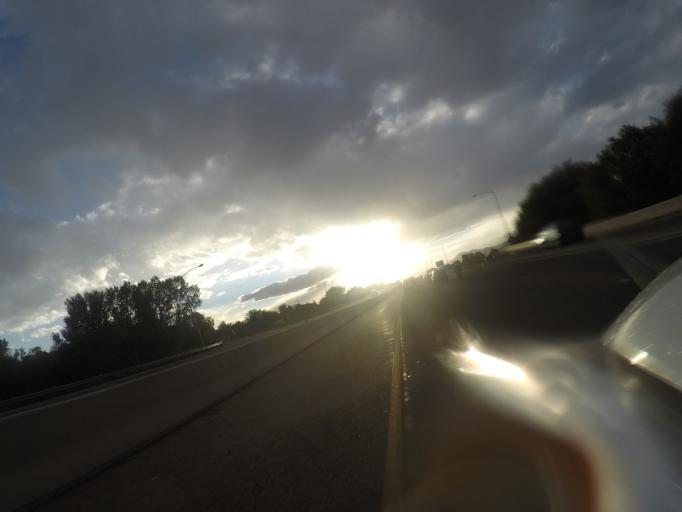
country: US
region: Colorado
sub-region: Arapahoe County
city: Sheridan
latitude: 39.6533
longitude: -105.0496
